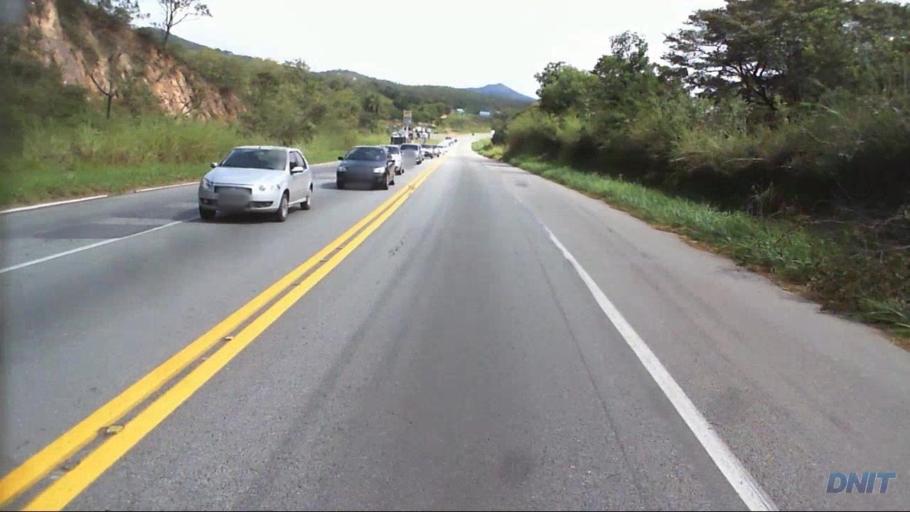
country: BR
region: Minas Gerais
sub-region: Santa Luzia
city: Santa Luzia
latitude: -19.8108
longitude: -43.7951
